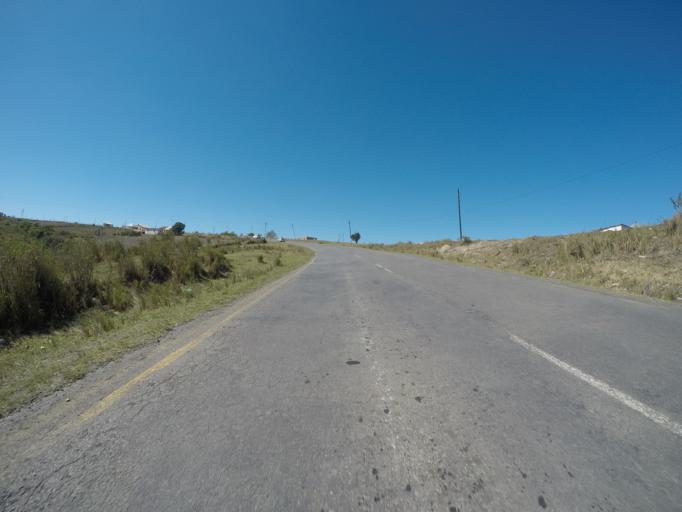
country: ZA
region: Eastern Cape
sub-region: OR Tambo District Municipality
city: Mthatha
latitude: -31.9195
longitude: 28.9673
